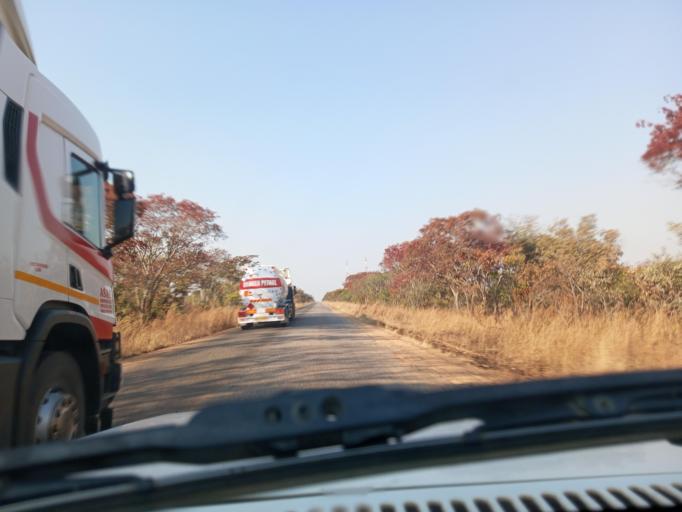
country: ZM
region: Northern
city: Mpika
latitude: -12.4115
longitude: 31.0837
